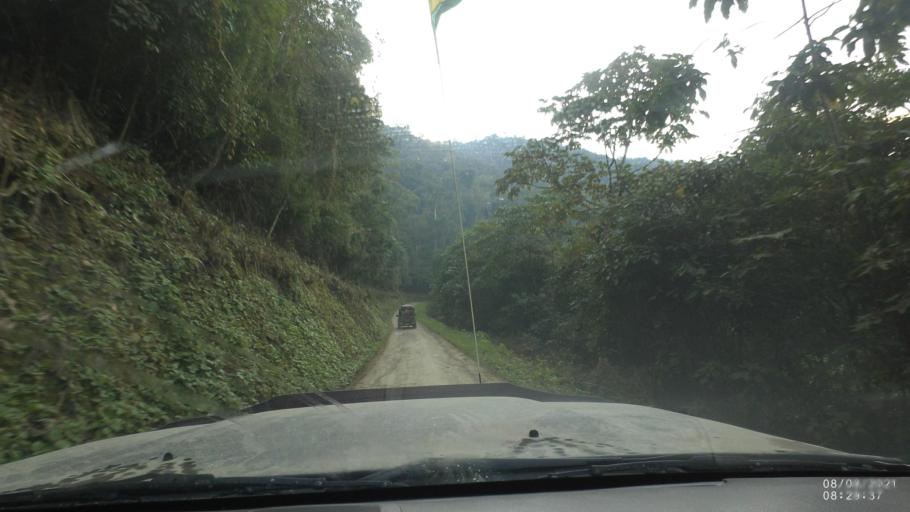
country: BO
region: La Paz
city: Quime
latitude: -16.5007
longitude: -66.7655
